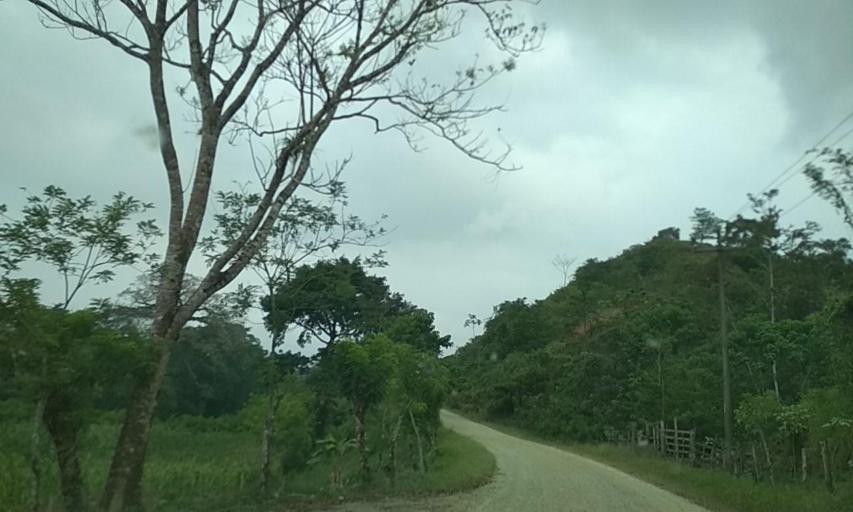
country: MX
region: Veracruz
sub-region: Uxpanapa
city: Poblado 10
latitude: 17.4529
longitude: -94.0878
